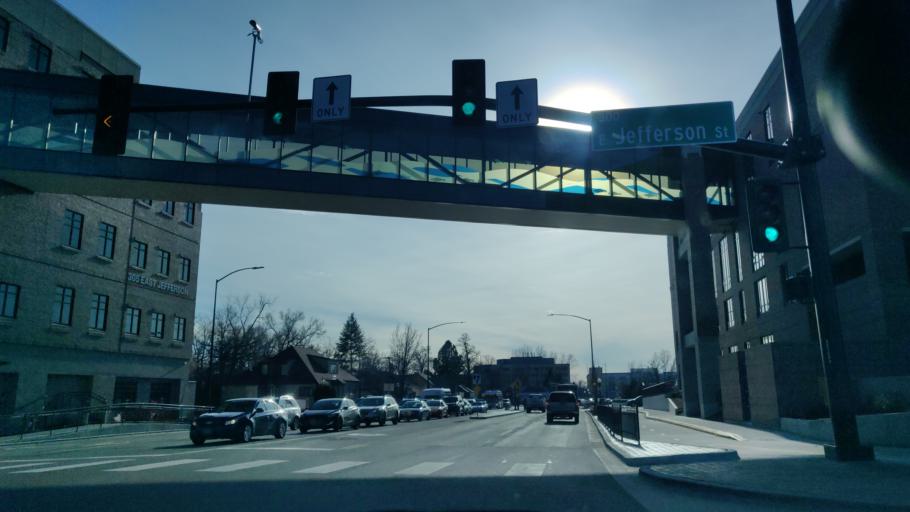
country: US
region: Idaho
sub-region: Ada County
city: Boise
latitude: 43.6127
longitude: -116.1909
